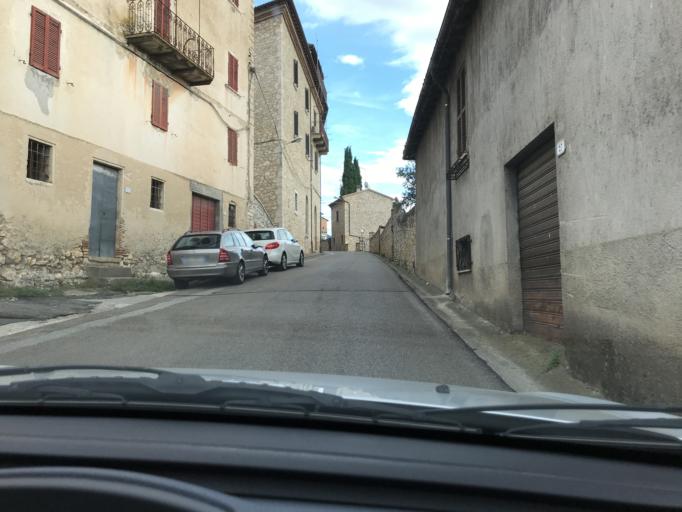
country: IT
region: Umbria
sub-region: Provincia di Terni
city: Montecchio
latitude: 42.6629
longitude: 12.2845
